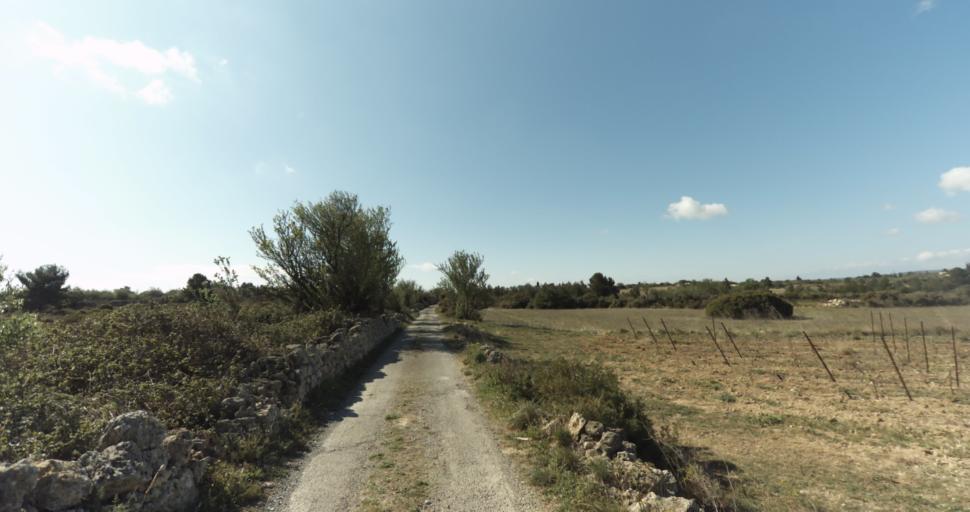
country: FR
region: Languedoc-Roussillon
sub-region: Departement de l'Aude
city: Leucate
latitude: 42.9266
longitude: 3.0312
